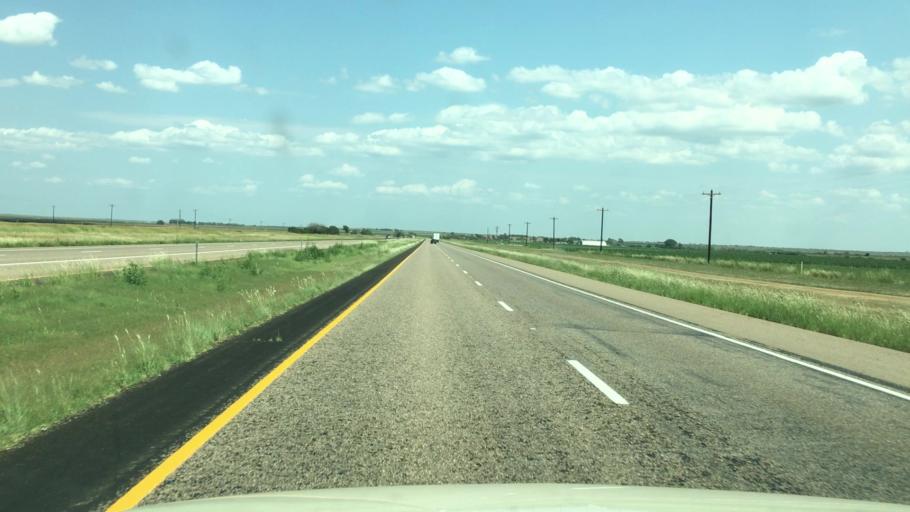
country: US
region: Texas
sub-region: Donley County
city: Clarendon
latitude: 35.0314
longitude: -101.1150
